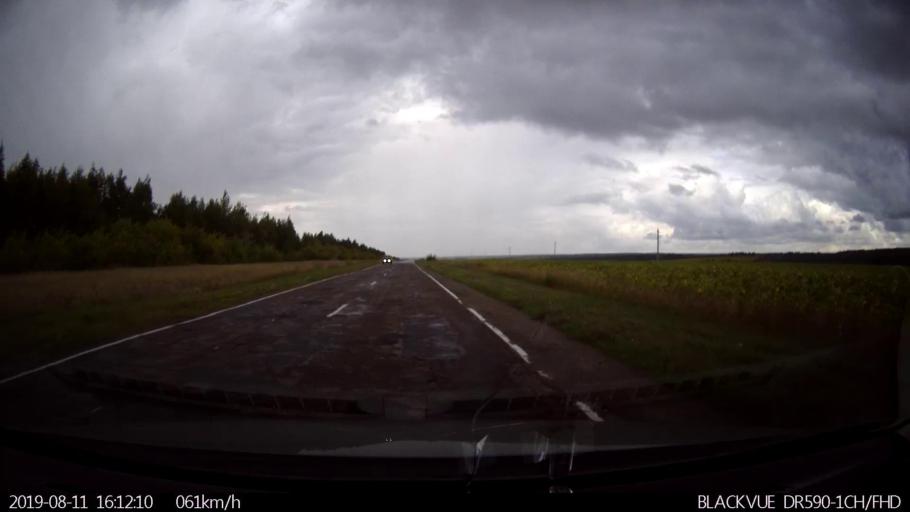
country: RU
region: Ulyanovsk
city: Ignatovka
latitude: 54.0092
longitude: 47.6413
